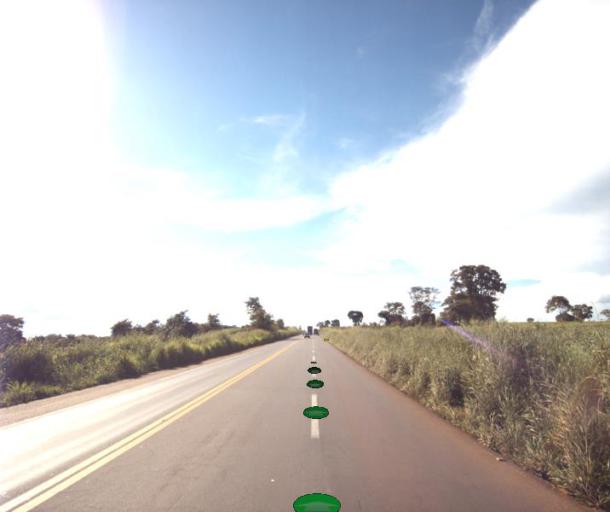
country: BR
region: Goias
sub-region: Rialma
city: Rialma
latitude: -15.3861
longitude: -49.5513
